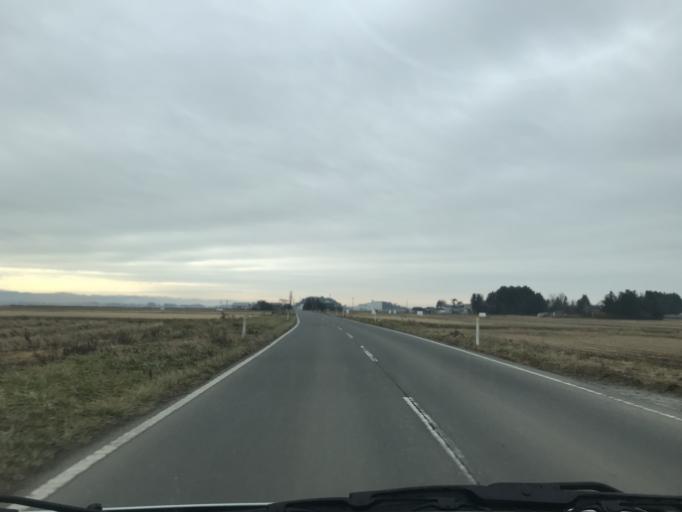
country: JP
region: Iwate
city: Ichinoseki
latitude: 38.7434
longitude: 141.2251
